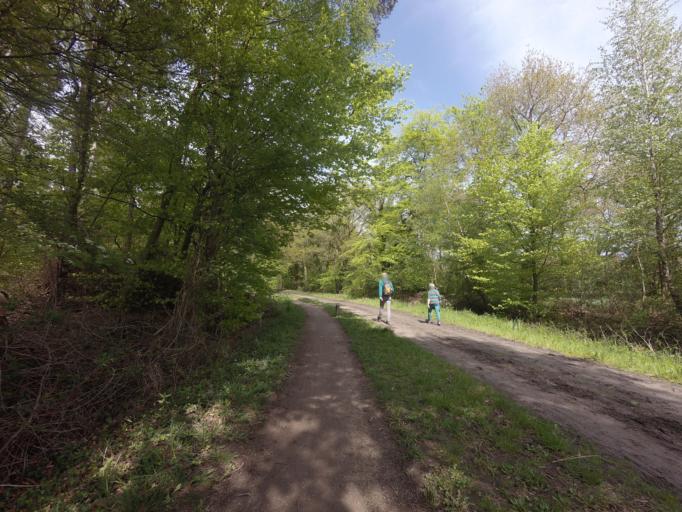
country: NL
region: Overijssel
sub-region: Gemeente Haaksbergen
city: Haaksbergen
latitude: 52.1303
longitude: 6.7148
